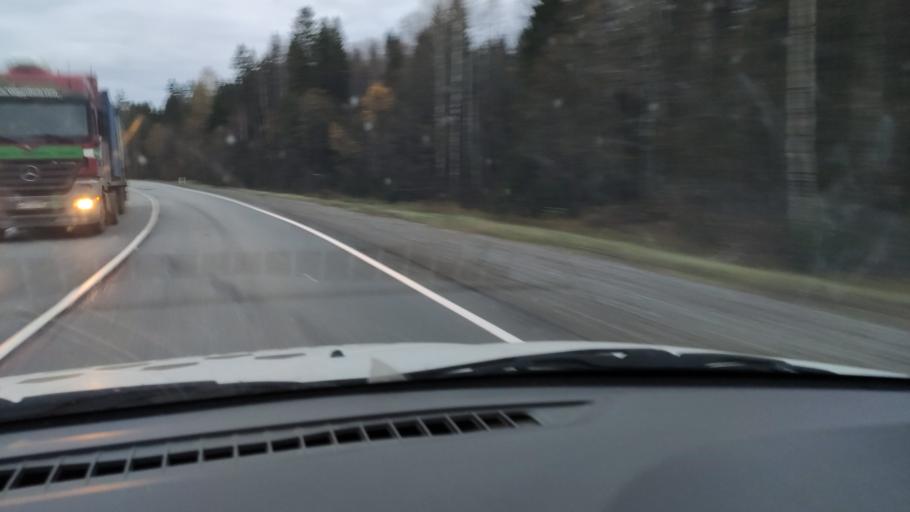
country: RU
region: Kirov
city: Kostino
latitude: 58.7936
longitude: 52.8762
